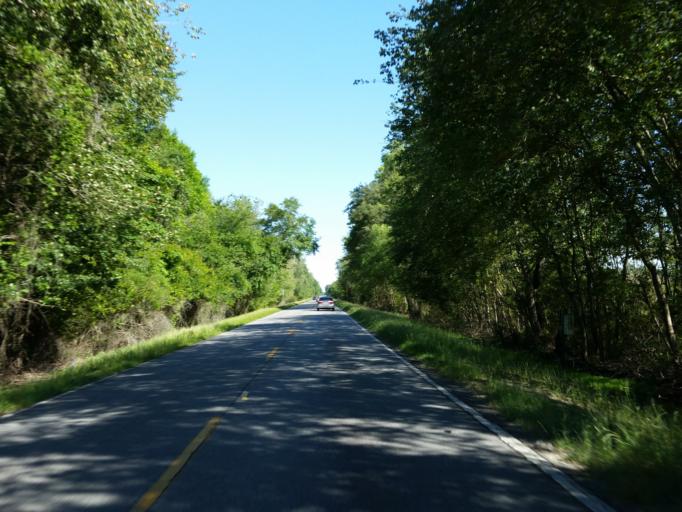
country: US
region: Georgia
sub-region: Echols County
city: Statenville
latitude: 30.6546
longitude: -83.1493
